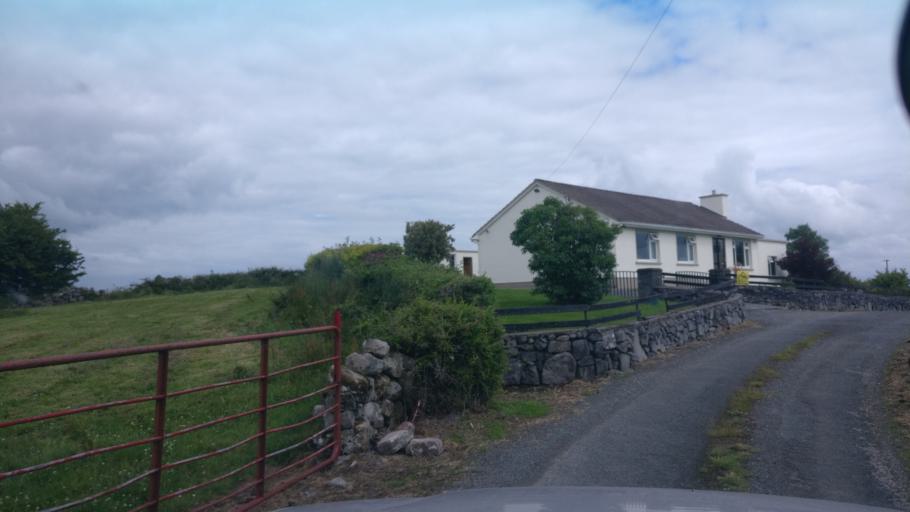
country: IE
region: Connaught
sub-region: County Galway
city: Loughrea
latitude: 53.1424
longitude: -8.5652
